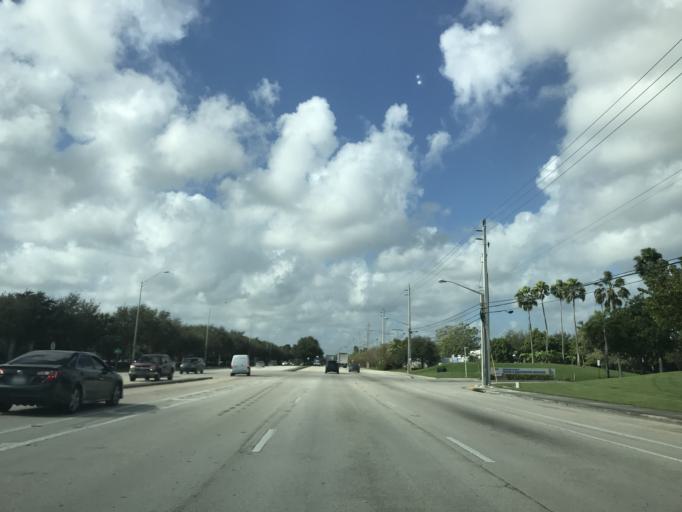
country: US
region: Florida
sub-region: Broward County
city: Coconut Creek
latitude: 26.2601
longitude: -80.1591
